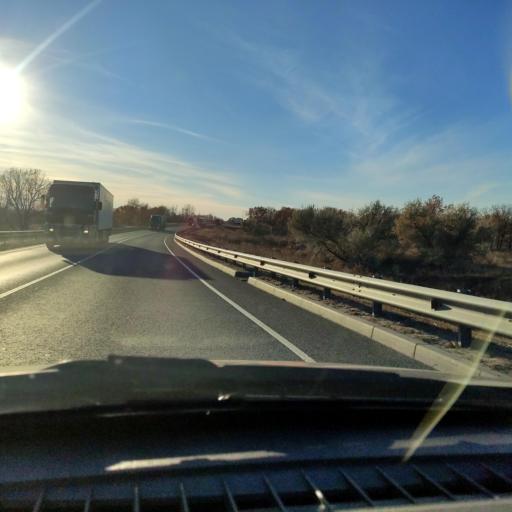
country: RU
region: Samara
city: Balasheyka
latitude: 53.1887
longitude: 48.2076
